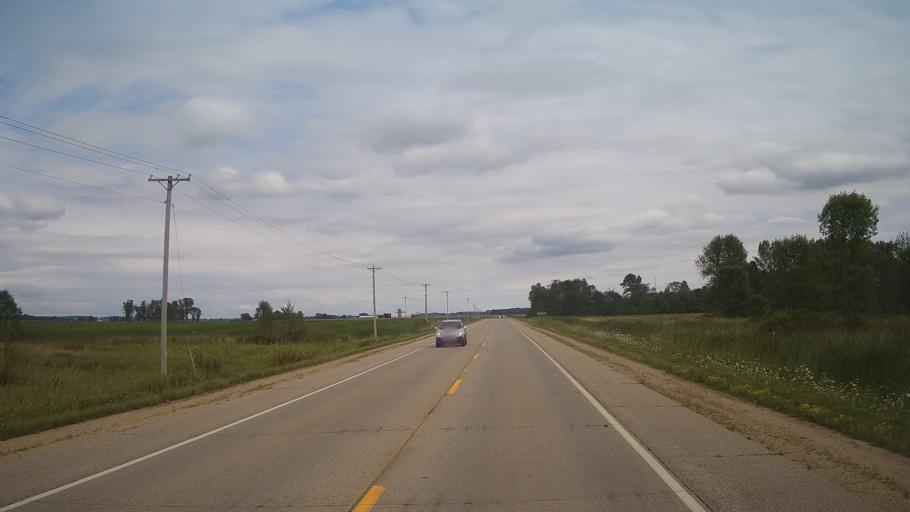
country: US
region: Wisconsin
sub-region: Waushara County
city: Redgranite
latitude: 44.0374
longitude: -89.0659
